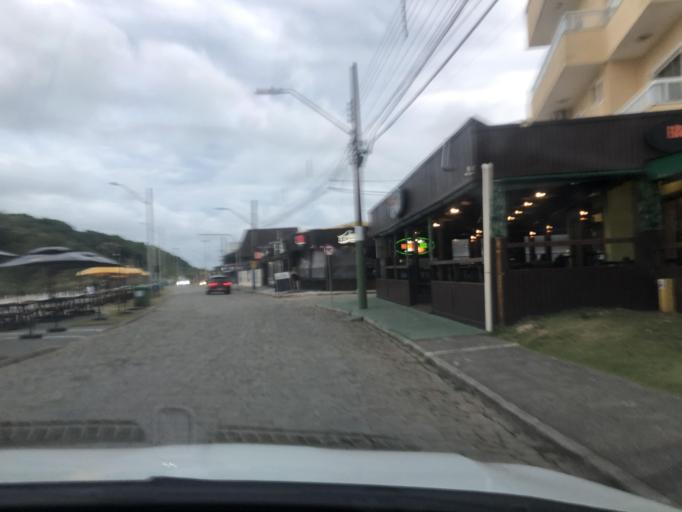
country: BR
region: Santa Catarina
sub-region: Sao Francisco Do Sul
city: Sao Francisco do Sul
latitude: -26.2316
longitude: -48.5011
